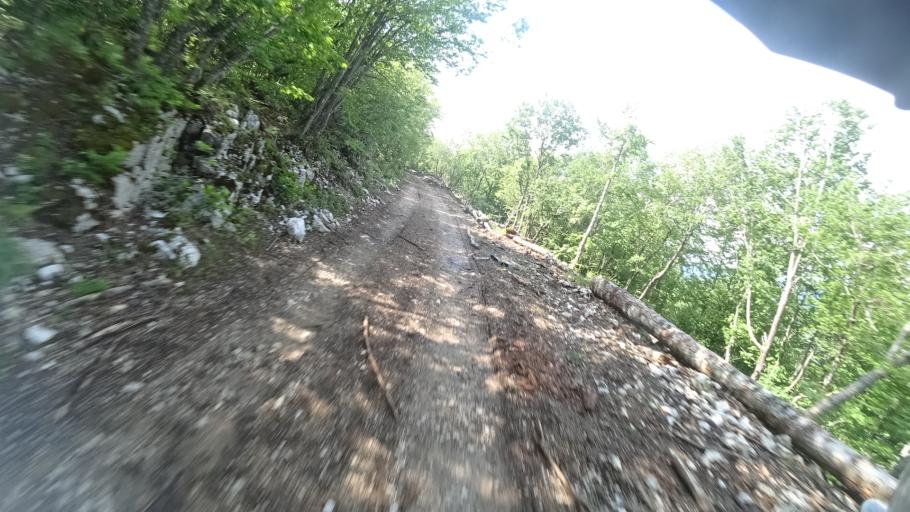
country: BA
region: Federation of Bosnia and Herzegovina
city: Izacic
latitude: 44.7688
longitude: 15.7496
